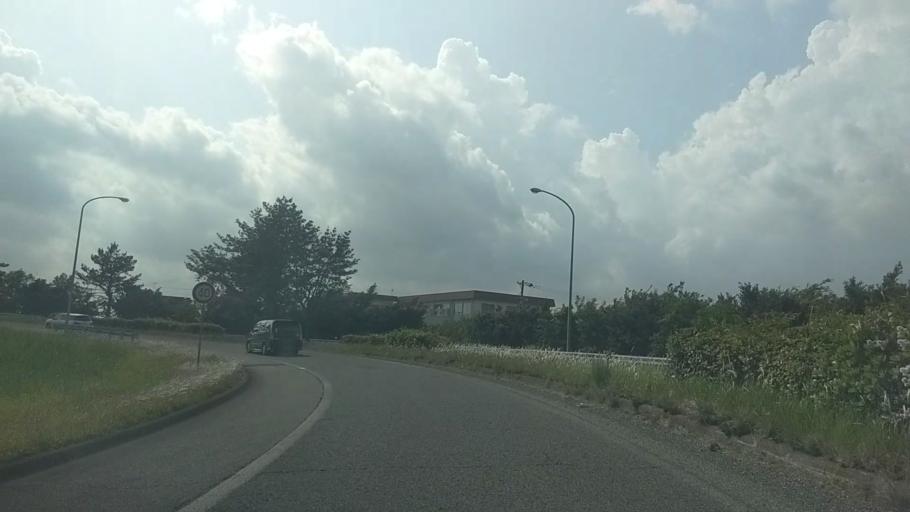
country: JP
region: Shizuoka
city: Hamakita
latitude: 34.7487
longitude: 137.7884
